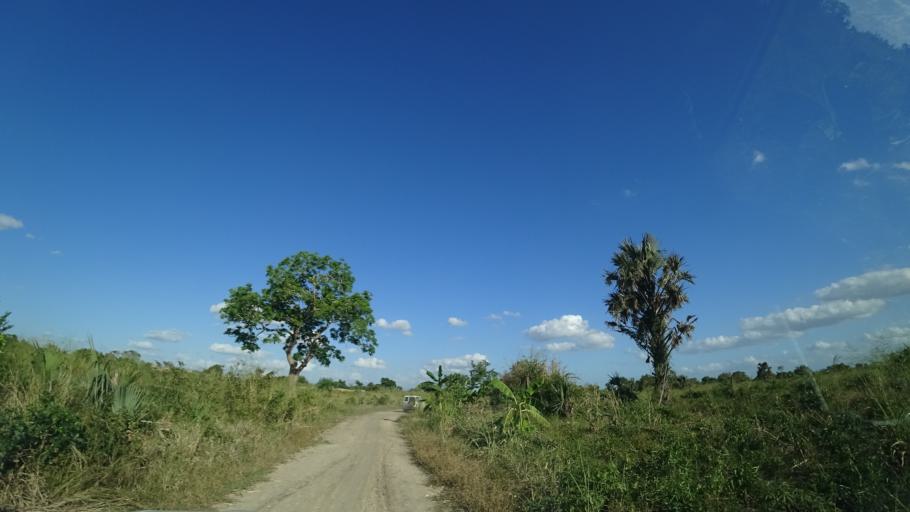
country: MZ
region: Sofala
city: Dondo
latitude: -19.3628
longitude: 34.5895
